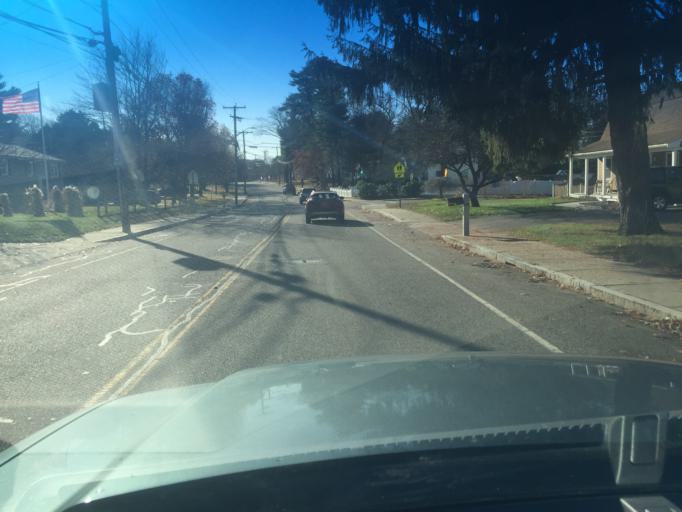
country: US
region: Massachusetts
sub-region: Norfolk County
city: Medway
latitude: 42.1147
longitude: -71.4300
